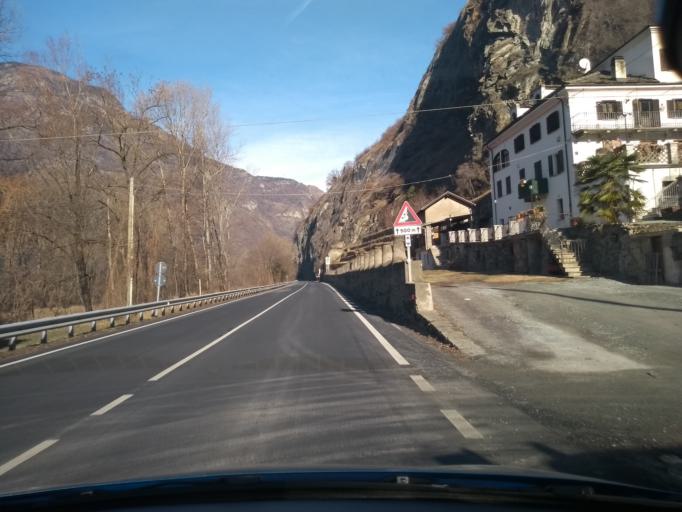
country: IT
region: Aosta Valley
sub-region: Valle d'Aosta
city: Champdepraz
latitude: 45.6832
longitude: 7.6741
